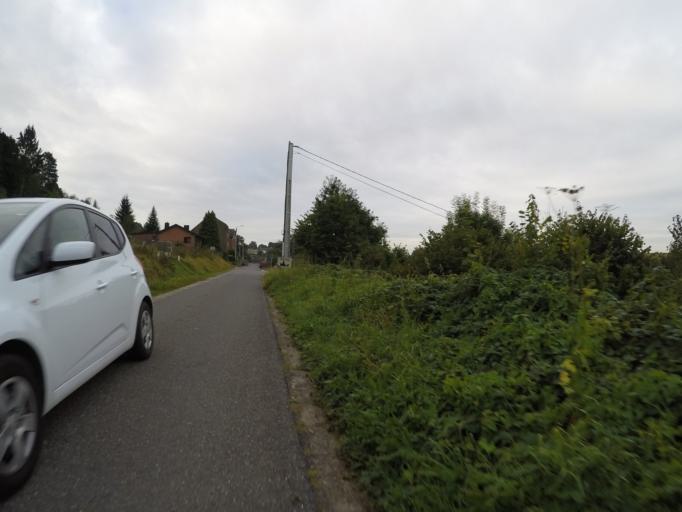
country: BE
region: Wallonia
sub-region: Province de Namur
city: Ciney
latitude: 50.3182
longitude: 5.0696
